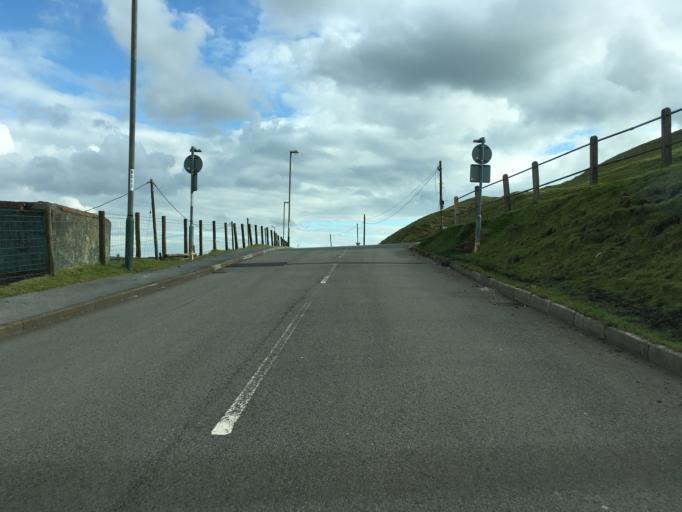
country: GB
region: Wales
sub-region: Caerphilly County Borough
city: Rhymney
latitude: 51.7342
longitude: -3.2992
